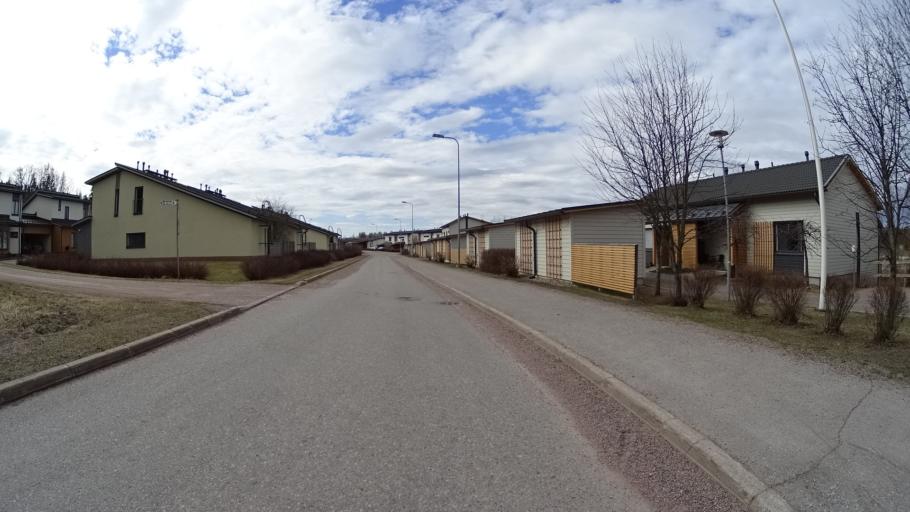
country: FI
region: Uusimaa
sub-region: Helsinki
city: Kauniainen
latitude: 60.2748
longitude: 24.7482
